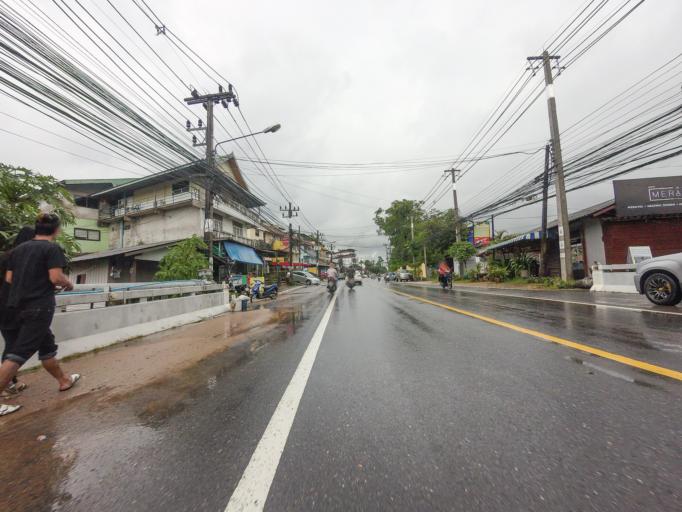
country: TH
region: Surat Thani
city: Ko Samui
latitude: 9.5118
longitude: 100.0514
